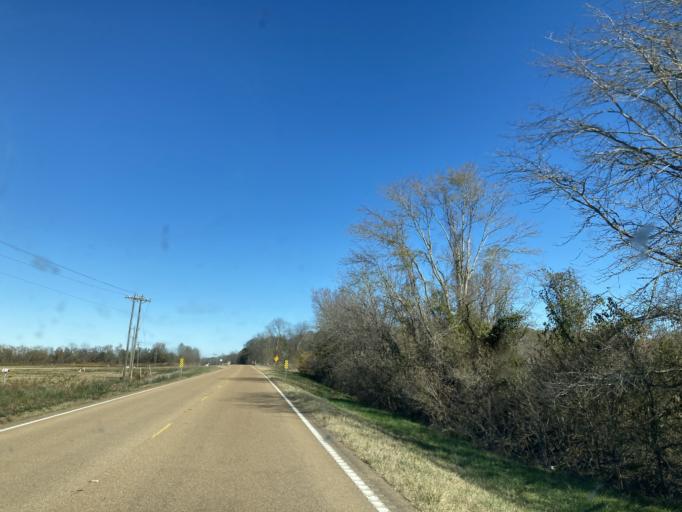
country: US
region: Mississippi
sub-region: Hinds County
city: Lynchburg
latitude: 32.6232
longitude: -90.5735
